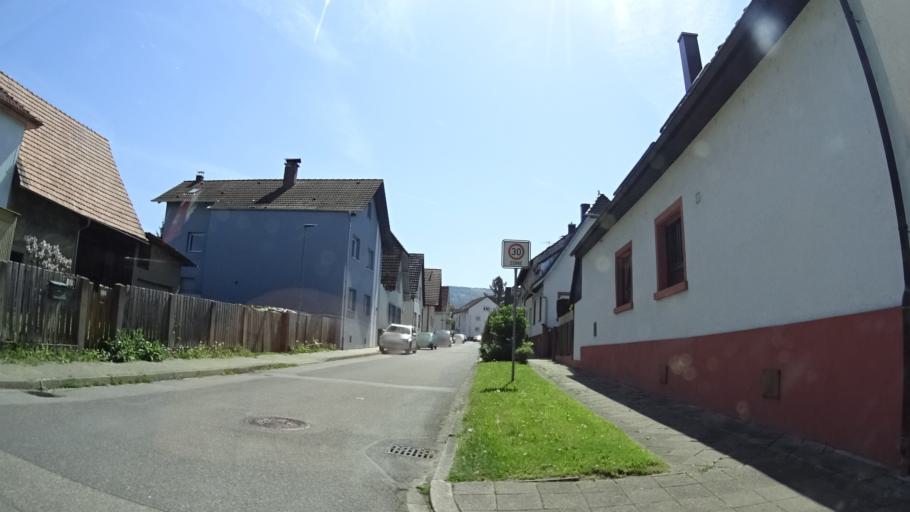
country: DE
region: Baden-Wuerttemberg
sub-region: Karlsruhe Region
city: Malsch
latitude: 48.8849
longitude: 8.3377
